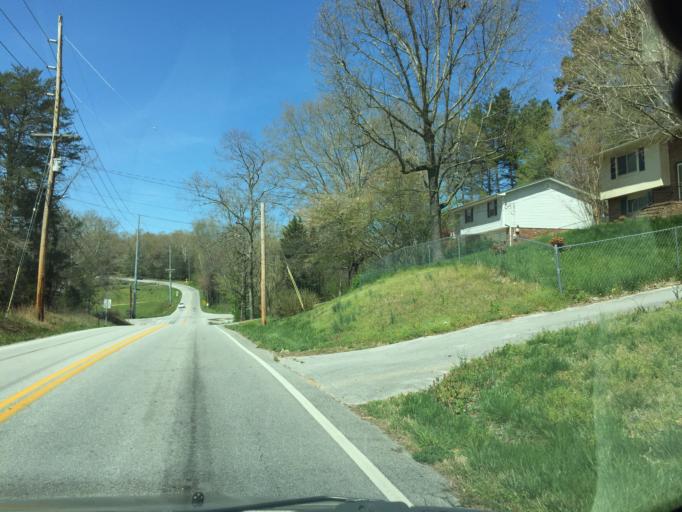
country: US
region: Tennessee
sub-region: Hamilton County
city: Middle Valley
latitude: 35.2018
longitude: -85.2064
